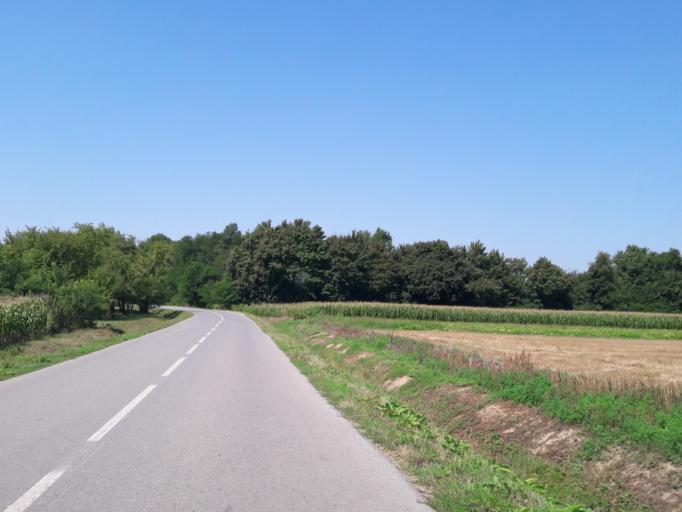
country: HR
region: Osjecko-Baranjska
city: Vuka
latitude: 45.4412
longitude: 18.4516
